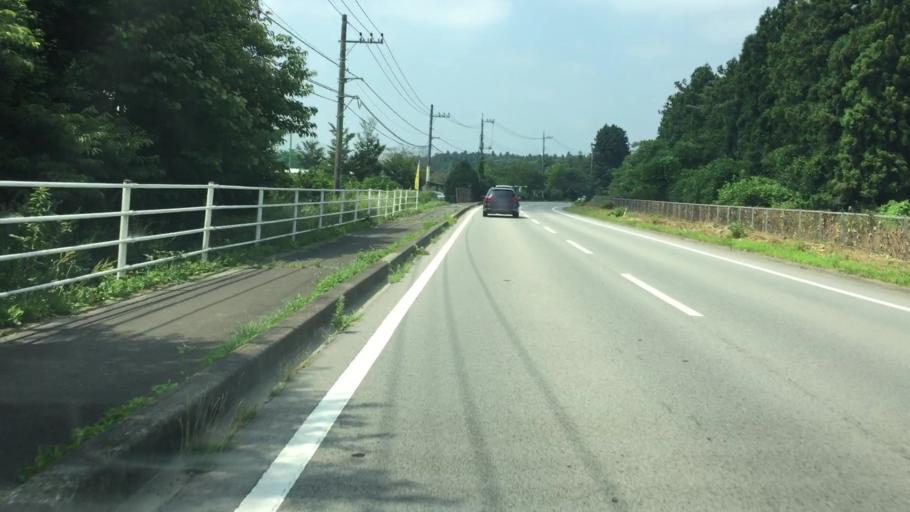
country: JP
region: Tochigi
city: Kuroiso
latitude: 37.0006
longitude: 139.9988
